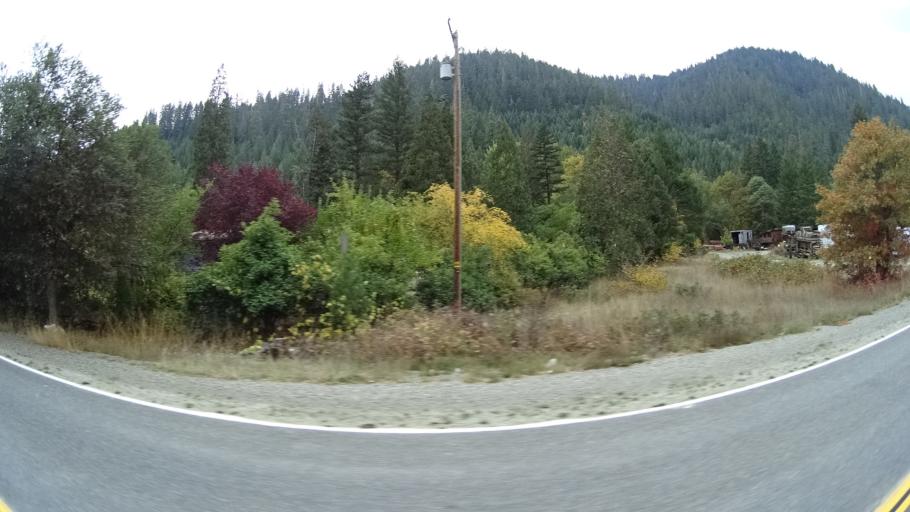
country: US
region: California
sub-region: Siskiyou County
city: Happy Camp
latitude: 41.8866
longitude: -123.4326
